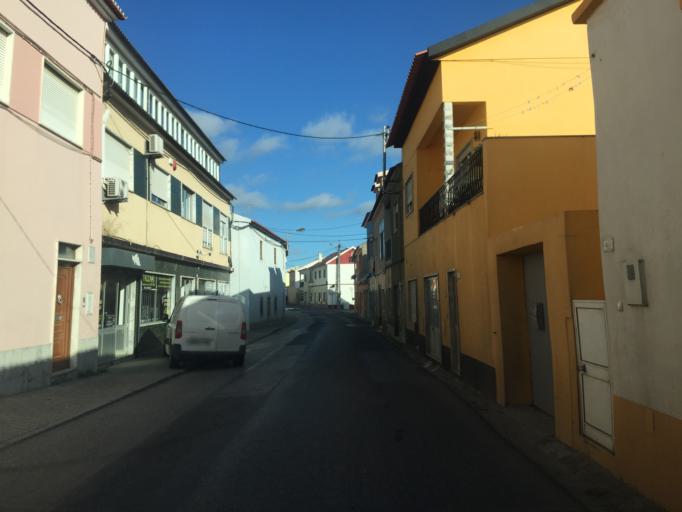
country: PT
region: Lisbon
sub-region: Torres Vedras
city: A dos Cunhados
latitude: 39.1502
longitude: -9.2971
